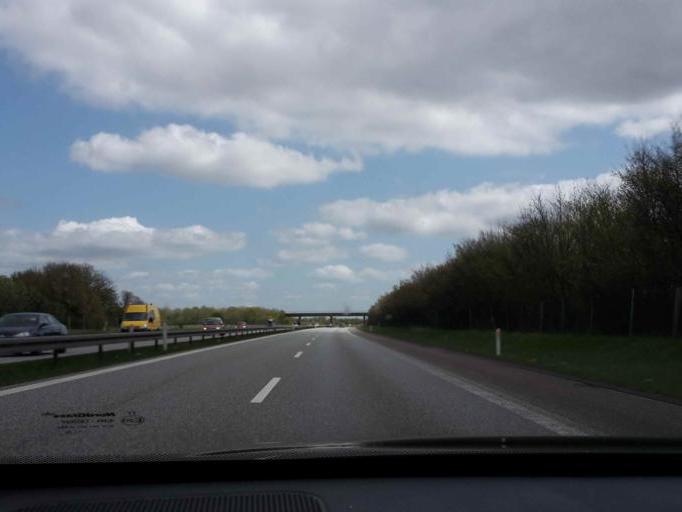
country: DK
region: South Denmark
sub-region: Esbjerg Kommune
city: Bramming
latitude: 55.5144
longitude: 8.7735
